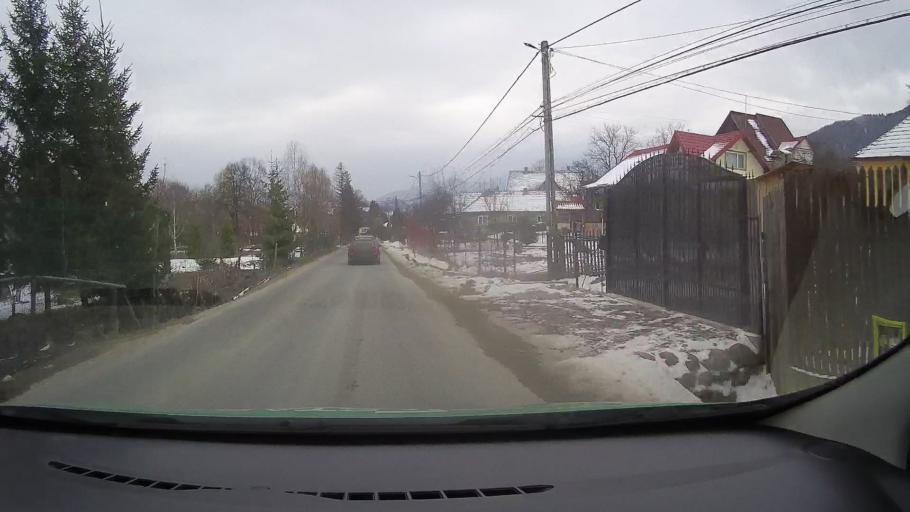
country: RO
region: Brasov
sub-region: Comuna Bran
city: Bran
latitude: 45.5304
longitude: 25.3520
